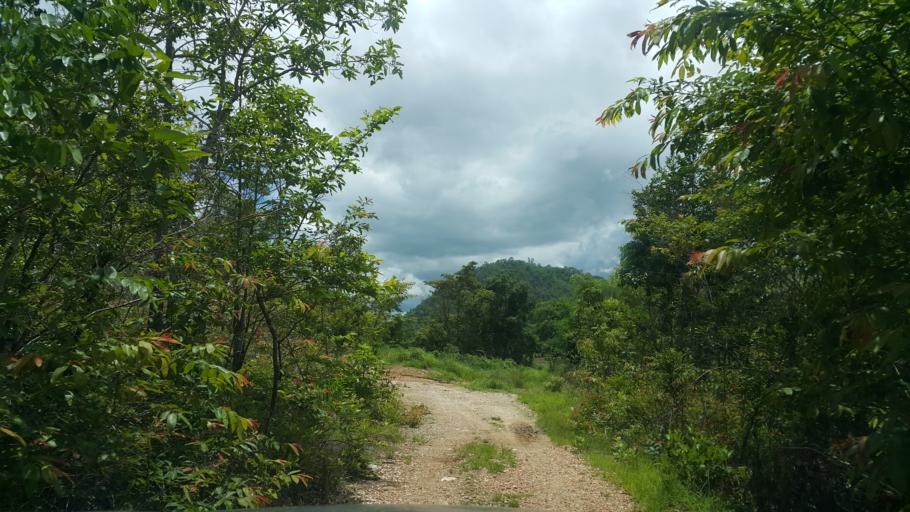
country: TH
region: Sukhothai
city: Thung Saliam
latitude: 17.3334
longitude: 99.4672
